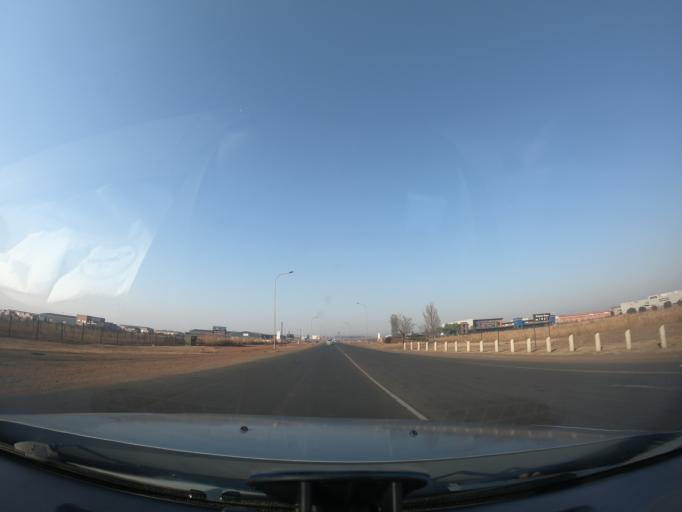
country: ZA
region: Mpumalanga
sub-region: Nkangala District Municipality
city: Middelburg
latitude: -25.8040
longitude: 29.4623
